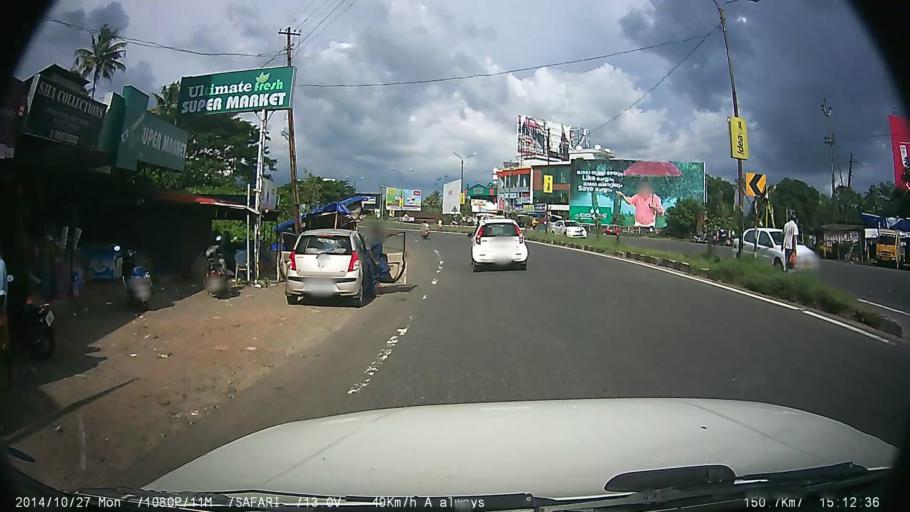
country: IN
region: Kerala
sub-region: Ernakulam
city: Aluva
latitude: 10.1301
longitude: 76.3516
